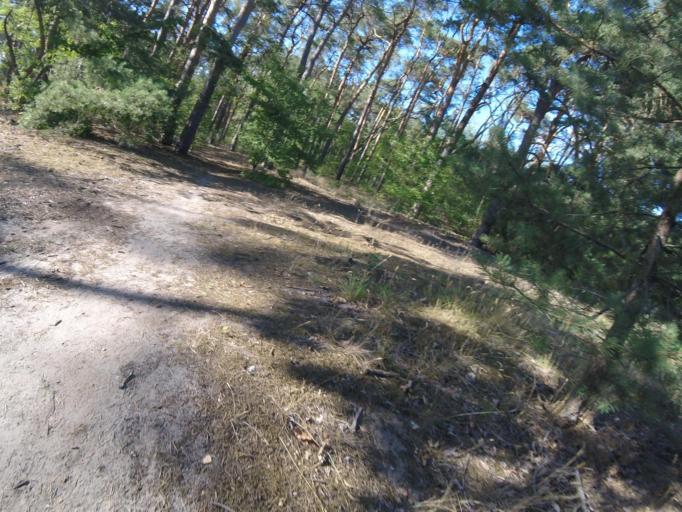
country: DE
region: Brandenburg
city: Konigs Wusterhausen
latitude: 52.3048
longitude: 13.6807
